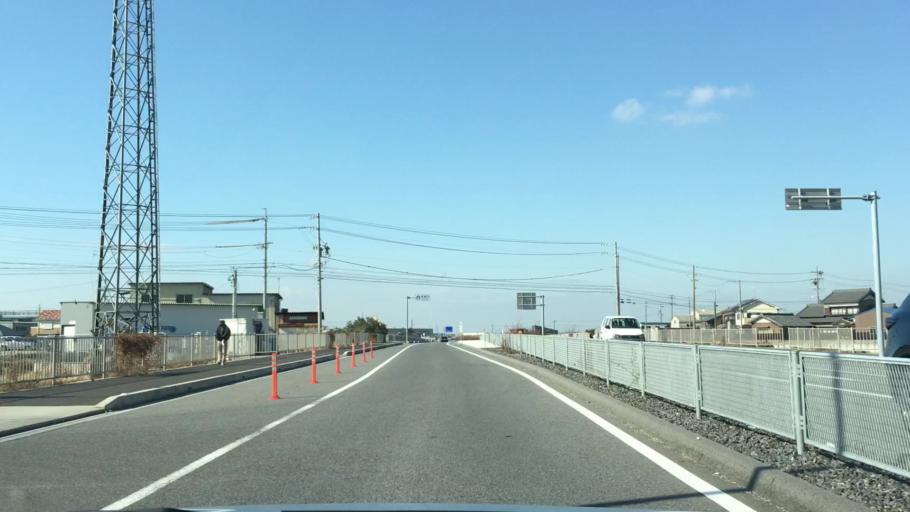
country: JP
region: Aichi
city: Anjo
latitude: 34.9917
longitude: 137.1169
